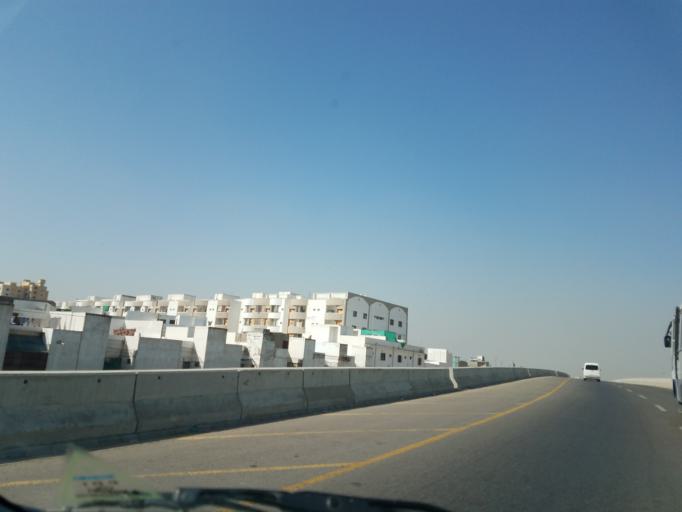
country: PK
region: Sindh
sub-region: Karachi District
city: Karachi
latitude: 24.9154
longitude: 67.0782
